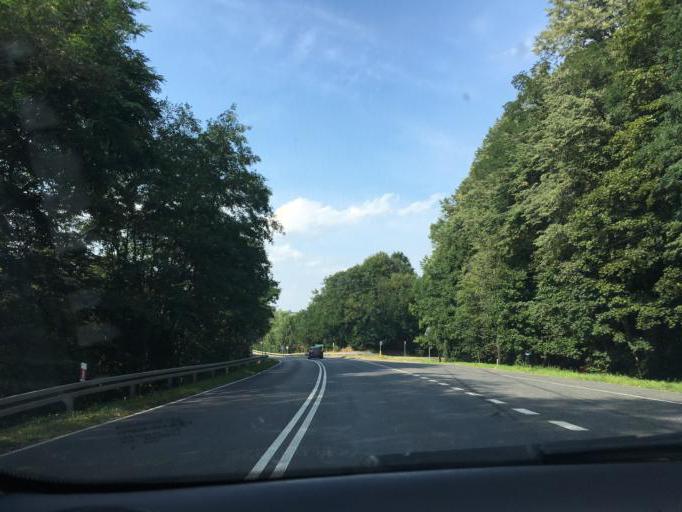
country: PL
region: Opole Voivodeship
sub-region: Powiat prudnicki
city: Laka Prudnicka
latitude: 50.4032
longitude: 17.5100
